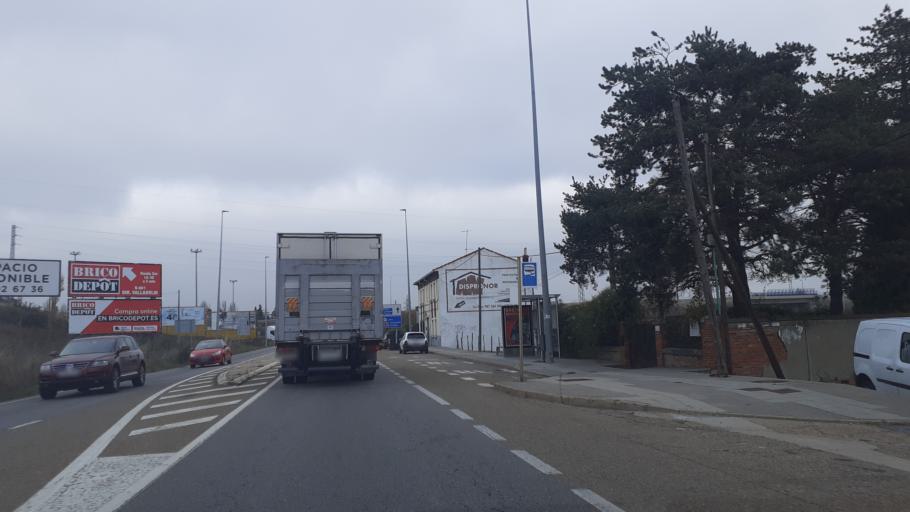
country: ES
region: Castille and Leon
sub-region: Provincia de Leon
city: Leon
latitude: 42.5668
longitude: -5.5824
